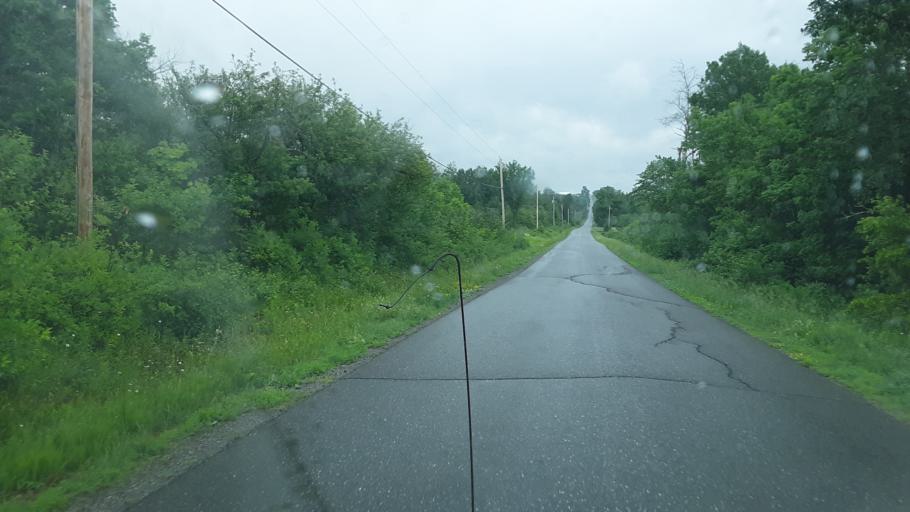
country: US
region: Maine
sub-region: Aroostook County
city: Presque Isle
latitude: 46.6813
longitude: -68.2134
